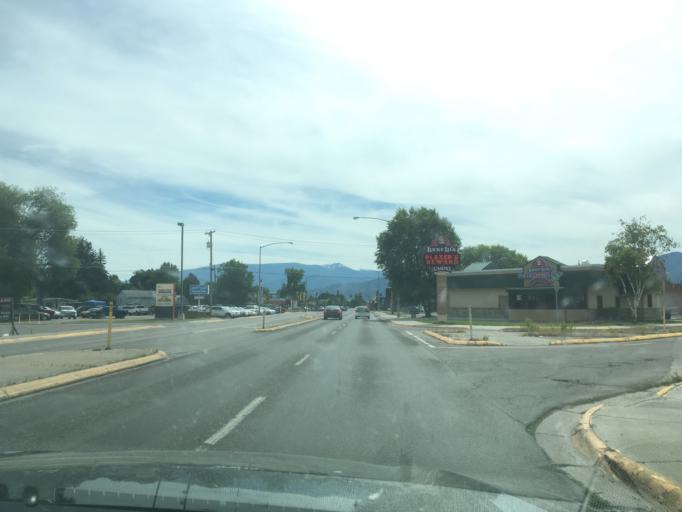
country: US
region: Montana
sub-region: Missoula County
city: Orchard Homes
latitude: 46.8428
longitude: -114.0269
